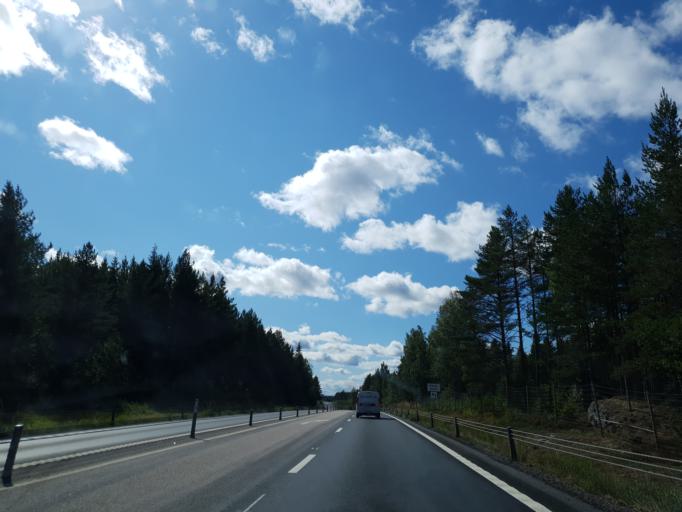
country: SE
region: Vaesterbotten
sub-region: Nordmalings Kommun
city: Nordmaling
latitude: 63.5149
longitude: 19.3636
